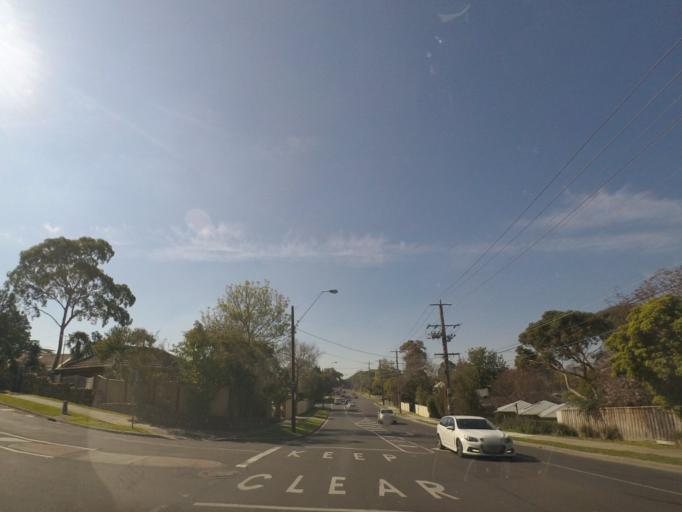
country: AU
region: Victoria
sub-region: Maroondah
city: Ringwood East
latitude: -37.8060
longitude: 145.2258
